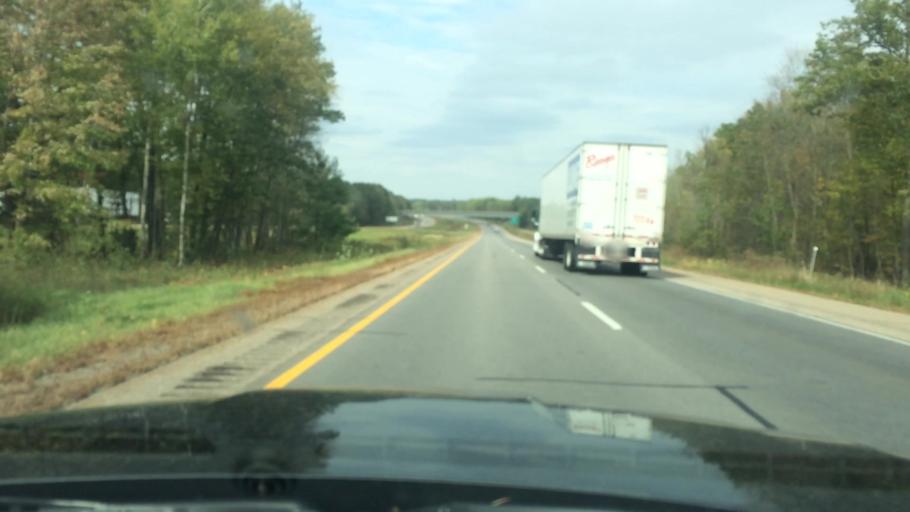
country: US
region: Wisconsin
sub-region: Marathon County
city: Mosinee
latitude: 44.7092
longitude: -89.6566
